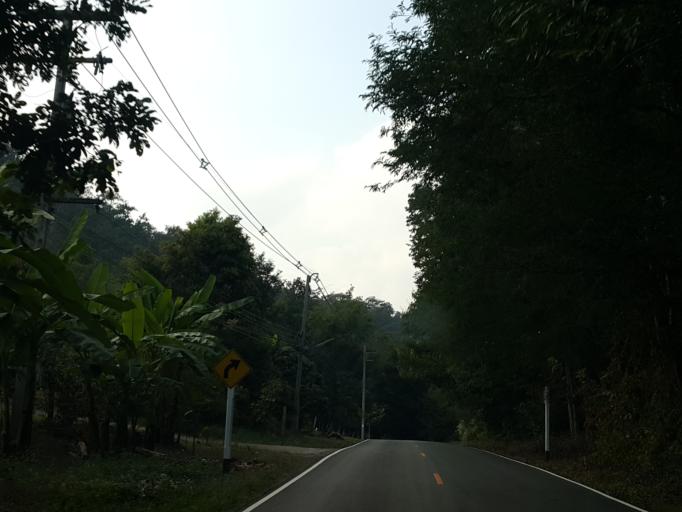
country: TH
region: Chiang Mai
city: Mae On
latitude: 18.9016
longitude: 99.2564
